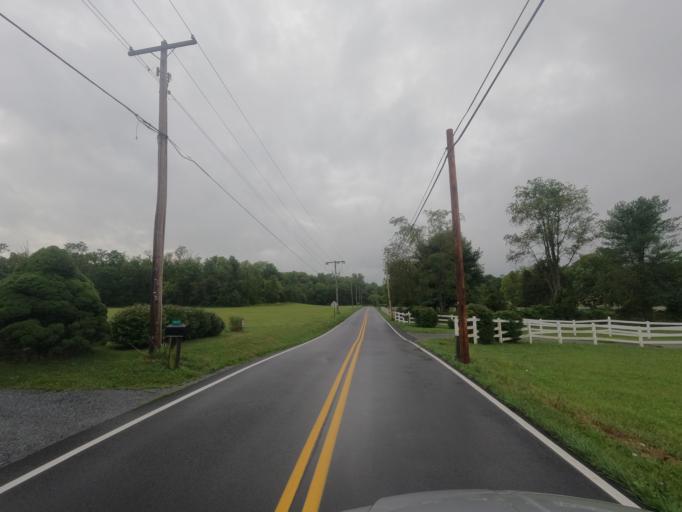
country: US
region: Maryland
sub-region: Washington County
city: Wilson-Conococheague
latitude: 39.6337
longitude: -77.9371
